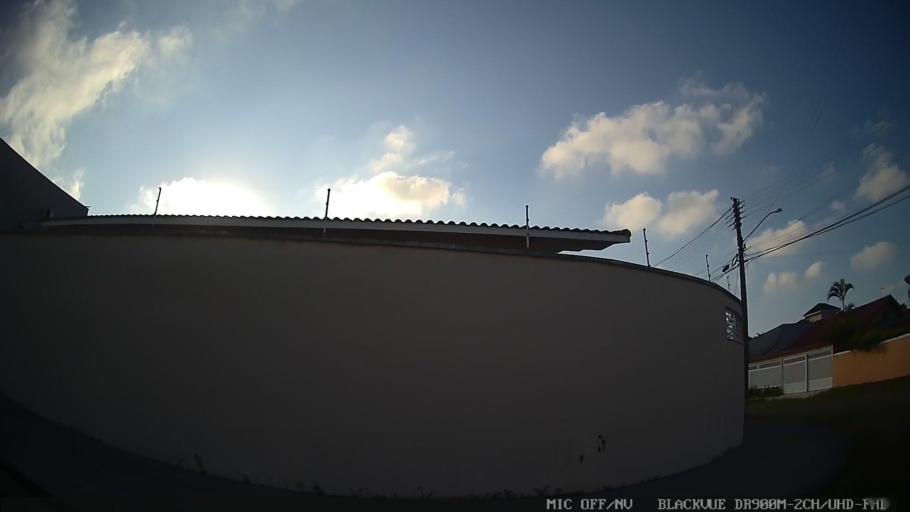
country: BR
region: Sao Paulo
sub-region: Peruibe
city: Peruibe
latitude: -24.2946
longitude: -46.9647
